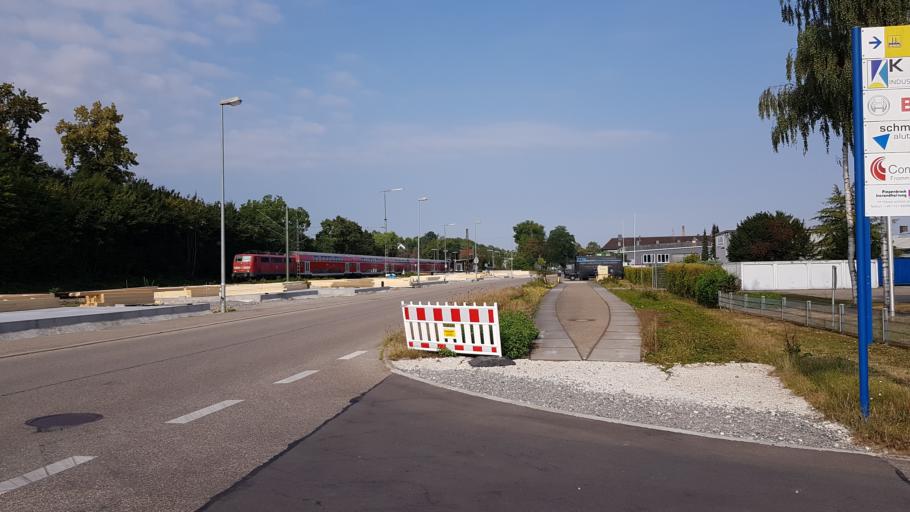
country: DE
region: Baden-Wuerttemberg
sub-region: Regierungsbezirk Stuttgart
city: Winterbach
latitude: 48.8102
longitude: 9.4237
